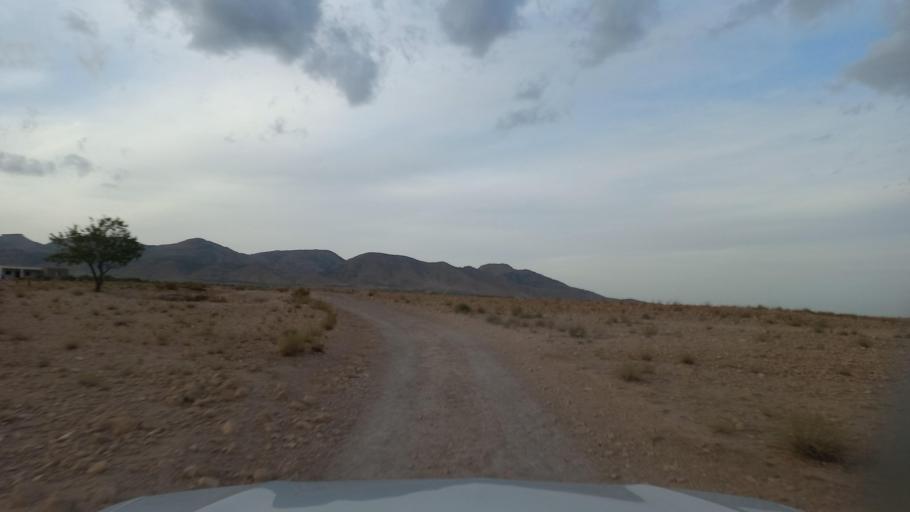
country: TN
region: Al Qasrayn
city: Sbiba
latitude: 35.4235
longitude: 9.0777
